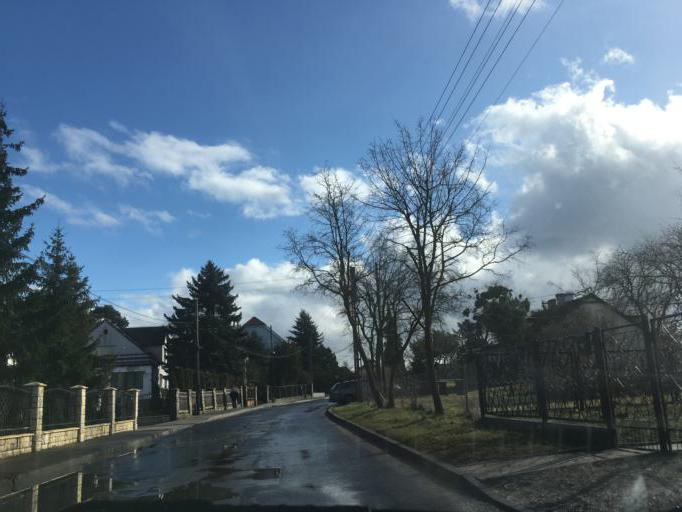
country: PL
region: Pomeranian Voivodeship
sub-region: Powiat gdanski
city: Cedry Wielkie
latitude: 54.3454
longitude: 18.8220
